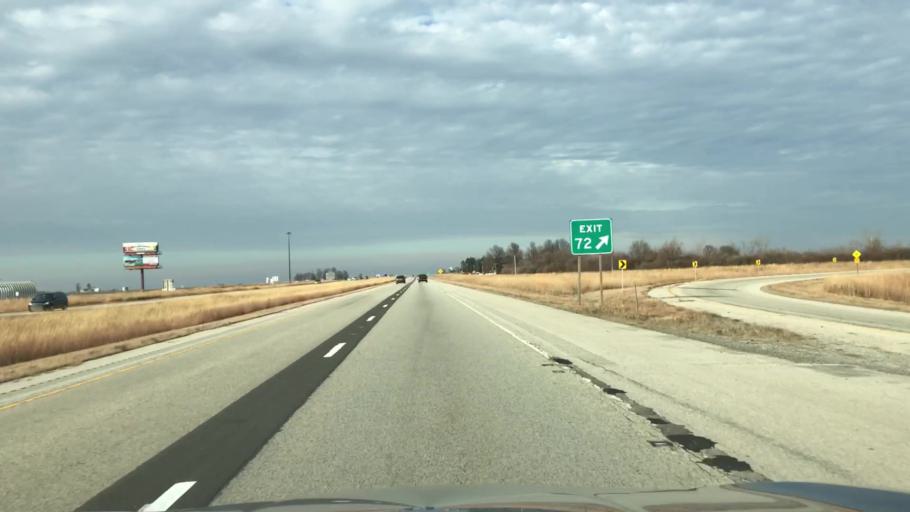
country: US
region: Illinois
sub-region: Sangamon County
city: Divernon
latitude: 39.4461
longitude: -89.6438
